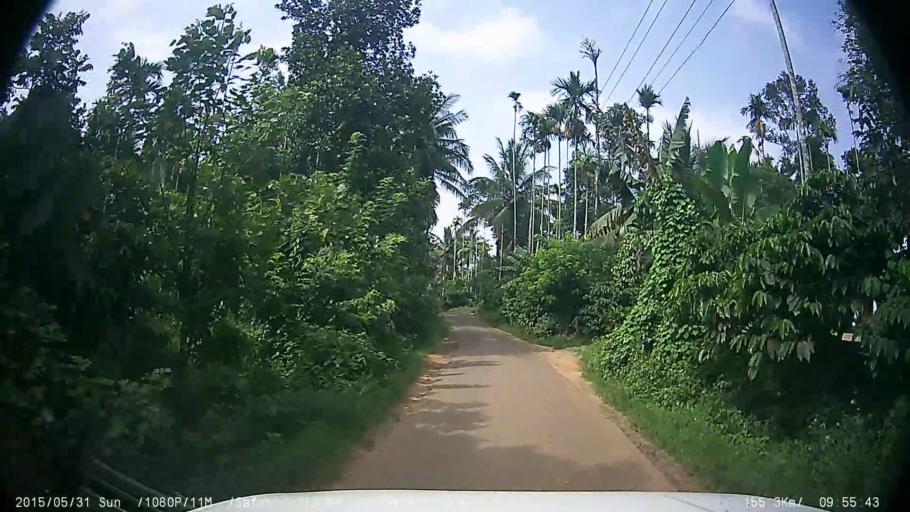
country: IN
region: Kerala
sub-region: Wayanad
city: Kalpetta
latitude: 11.6013
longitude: 76.0541
